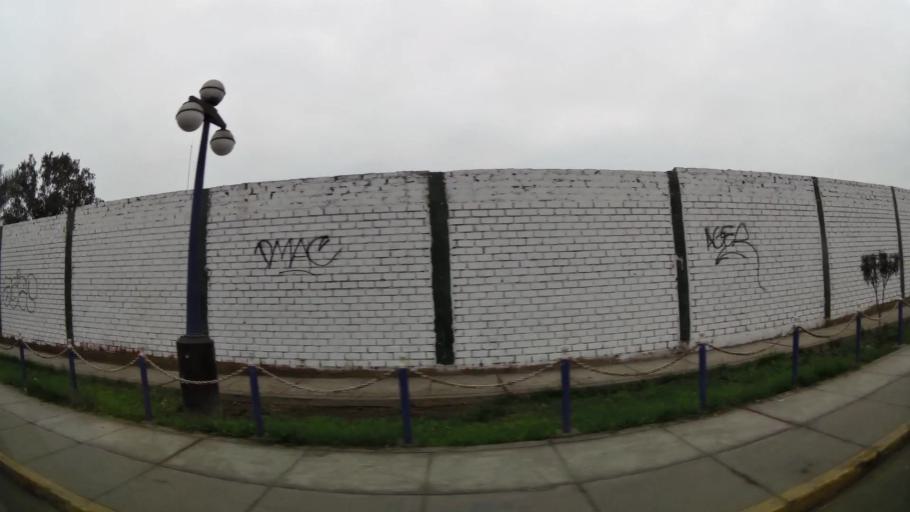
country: PE
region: Lima
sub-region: Lima
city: Surco
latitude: -12.1656
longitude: -77.0196
